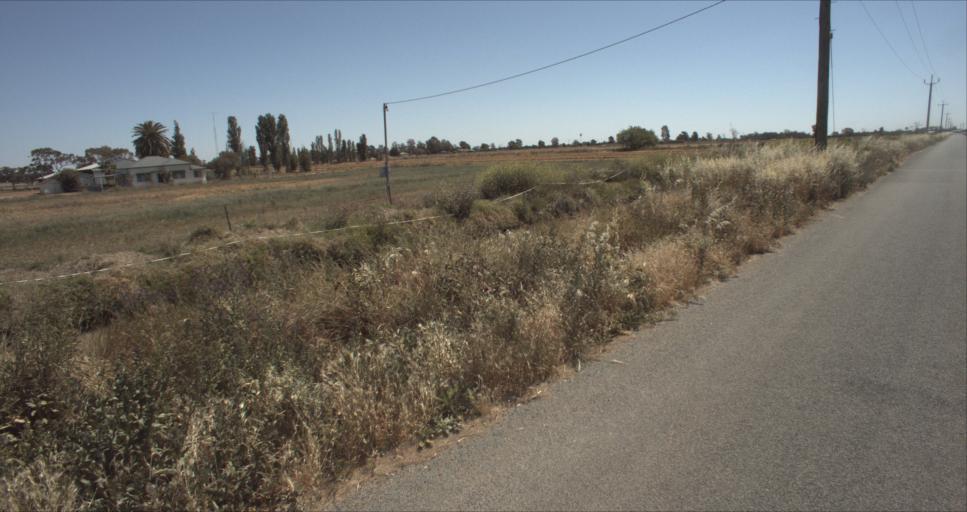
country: AU
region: New South Wales
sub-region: Leeton
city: Leeton
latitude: -34.5121
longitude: 146.4289
